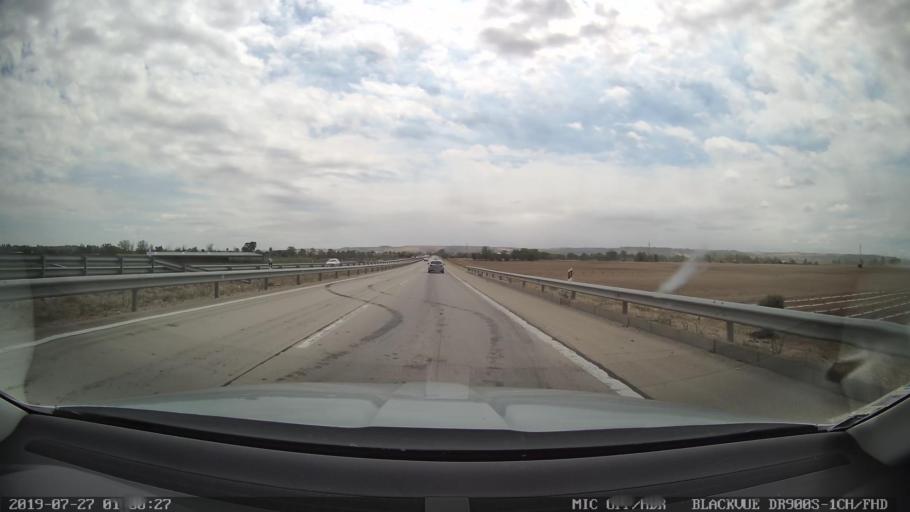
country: ES
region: Castille-La Mancha
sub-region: Province of Toledo
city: Talavera de la Reina
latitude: 39.9932
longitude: -4.7615
